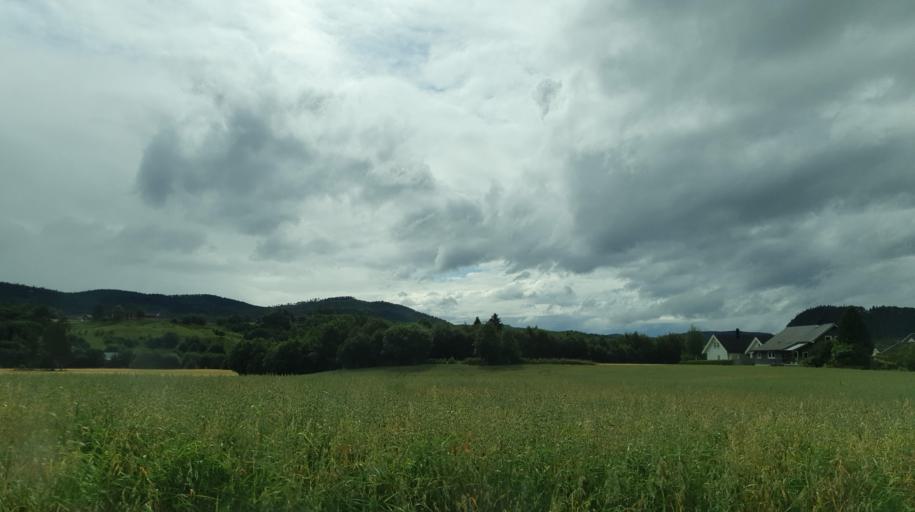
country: NO
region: Nord-Trondelag
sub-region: Stjordal
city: Stjordalshalsen
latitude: 63.4506
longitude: 10.9809
